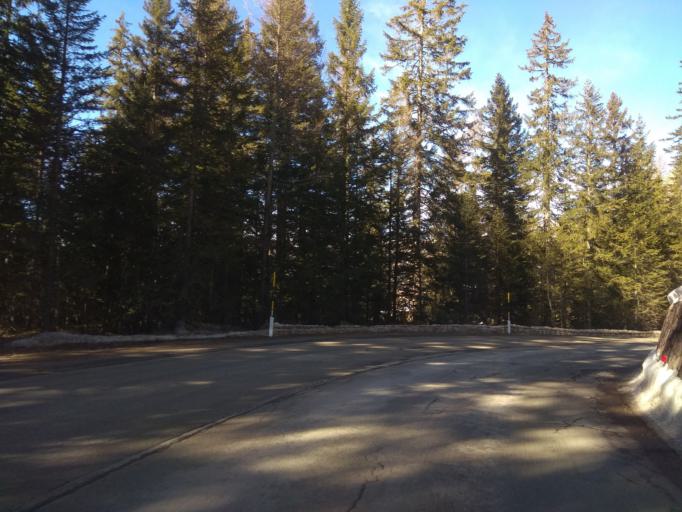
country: IT
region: Trentino-Alto Adige
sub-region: Bolzano
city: Nova Levante
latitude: 46.4405
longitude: 11.5891
